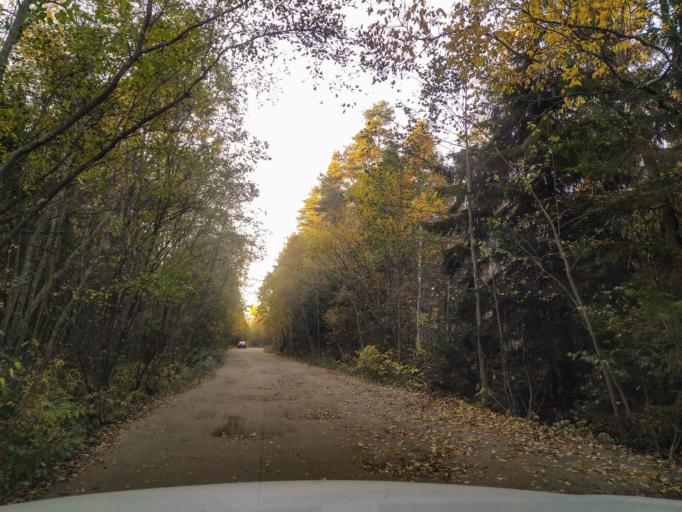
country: RU
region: Leningrad
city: Kuznechnoye
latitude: 61.3030
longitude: 30.0476
